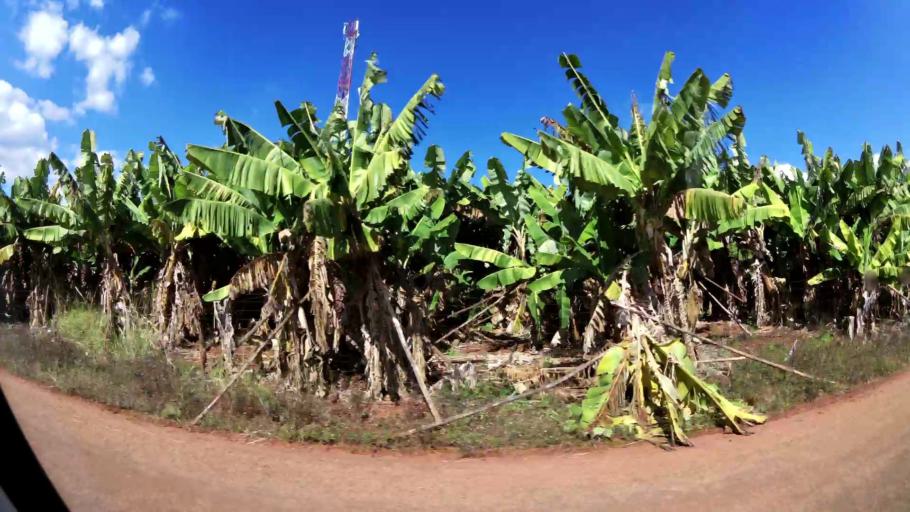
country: ZA
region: Limpopo
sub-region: Mopani District Municipality
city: Tzaneen
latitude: -23.7988
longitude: 30.1348
